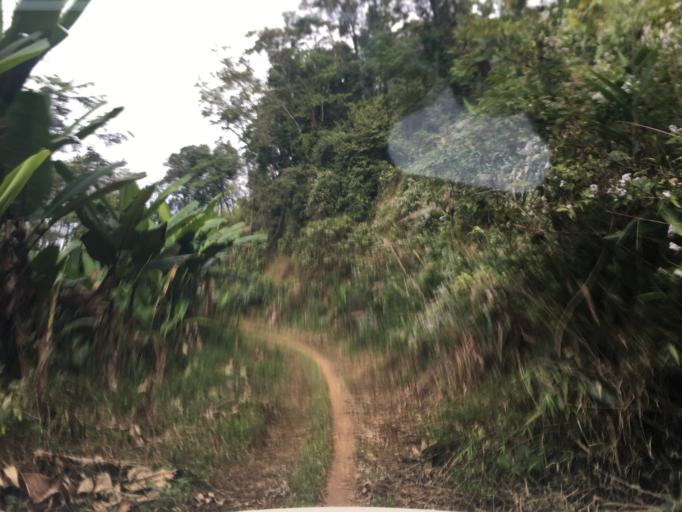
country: LA
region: Houaphan
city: Viengthong
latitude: 19.9162
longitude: 103.2994
